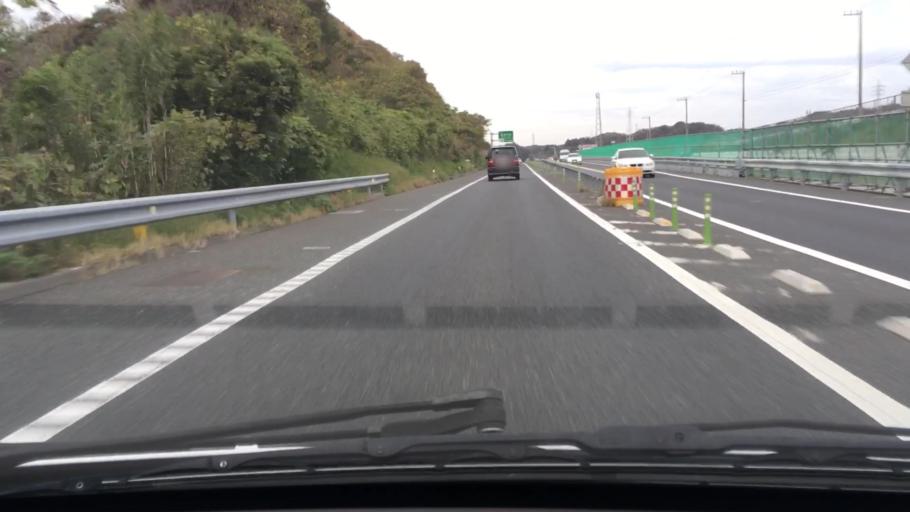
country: JP
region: Chiba
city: Kimitsu
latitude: 35.2427
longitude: 139.8889
